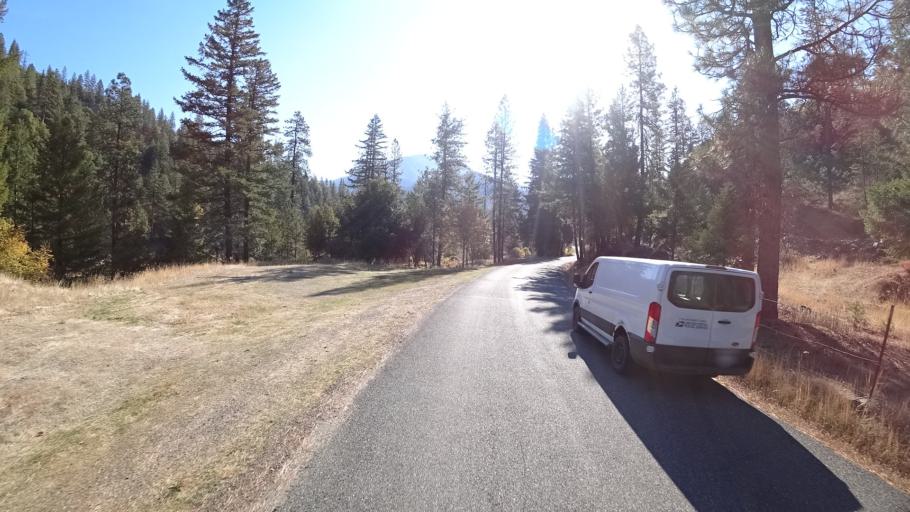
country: US
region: California
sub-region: Siskiyou County
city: Yreka
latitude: 41.7459
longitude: -123.0066
